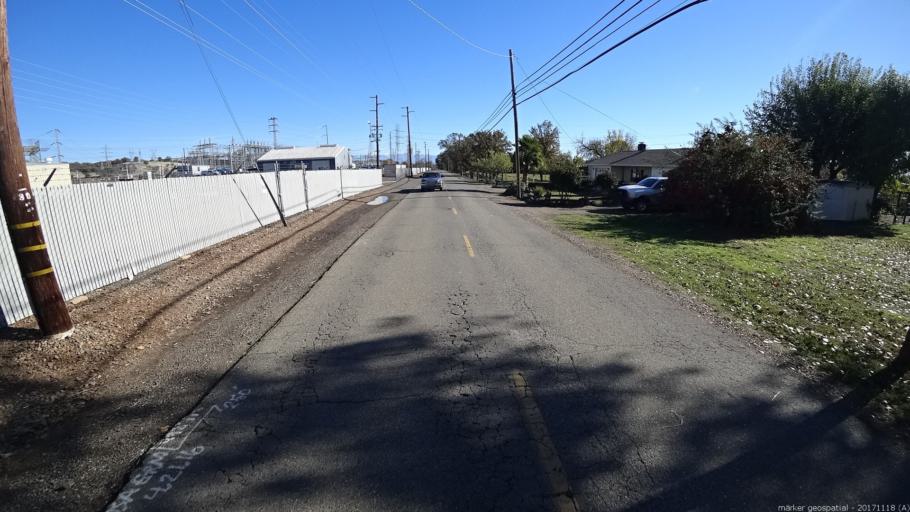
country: US
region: California
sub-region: Shasta County
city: Cottonwood
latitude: 40.3966
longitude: -122.2677
